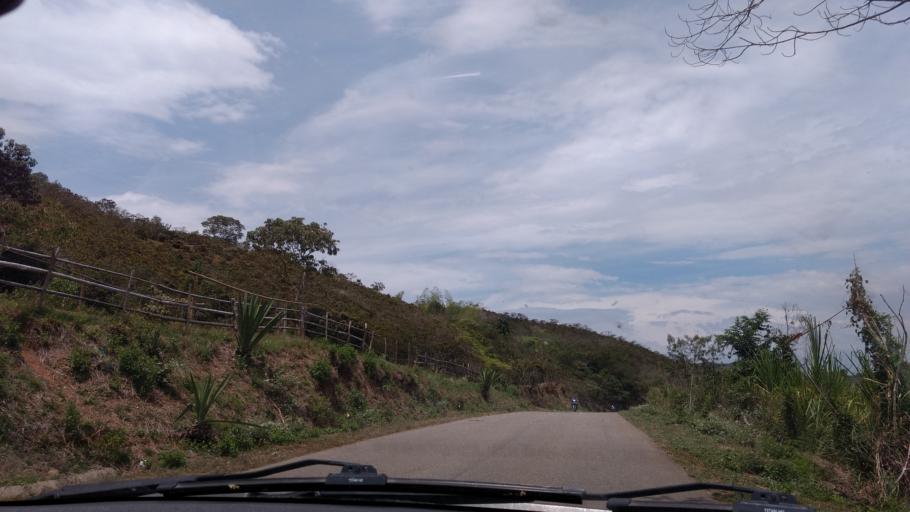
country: CO
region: Cauca
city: Buenos Aires
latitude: 3.0460
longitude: -76.6645
